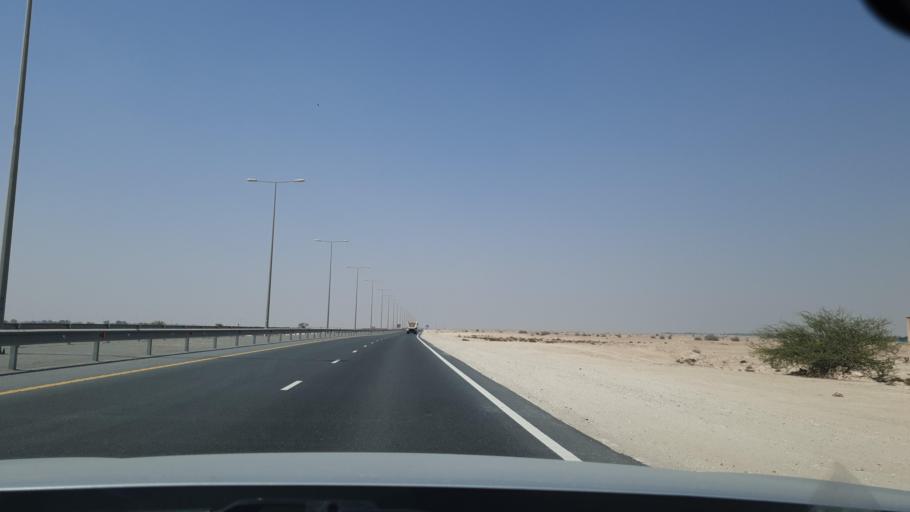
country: QA
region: Baladiyat az Za`ayin
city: Az Za`ayin
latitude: 25.6202
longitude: 51.3506
